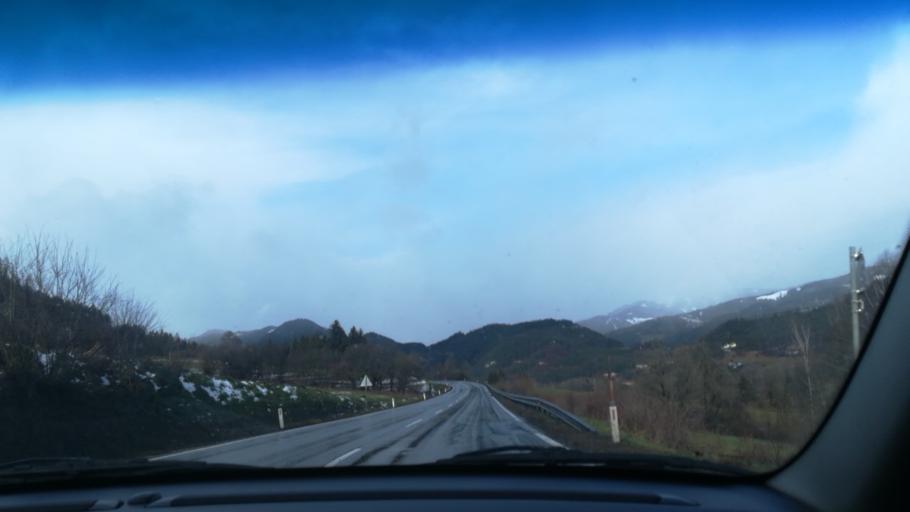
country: AT
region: Styria
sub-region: Politischer Bezirk Murtal
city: Sankt Peter ob Judenburg
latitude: 47.1908
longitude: 14.5840
